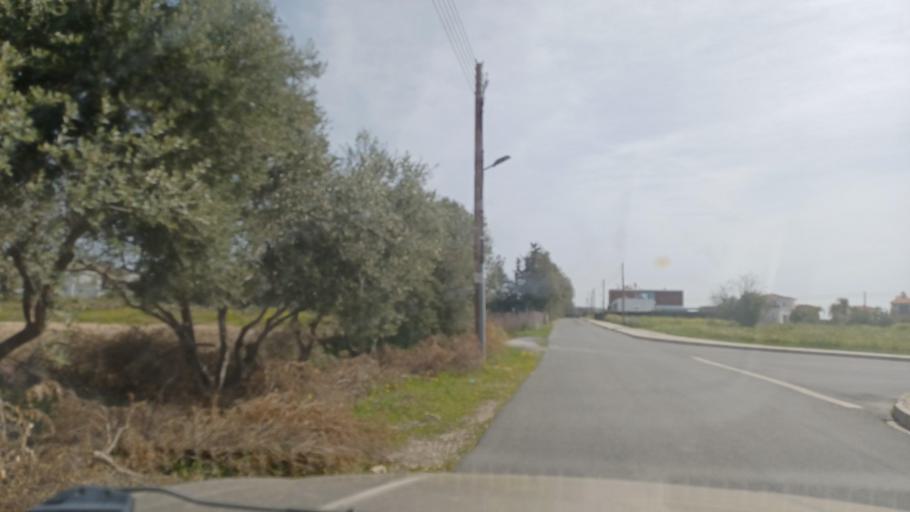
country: CY
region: Pafos
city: Paphos
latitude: 34.7536
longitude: 32.4694
